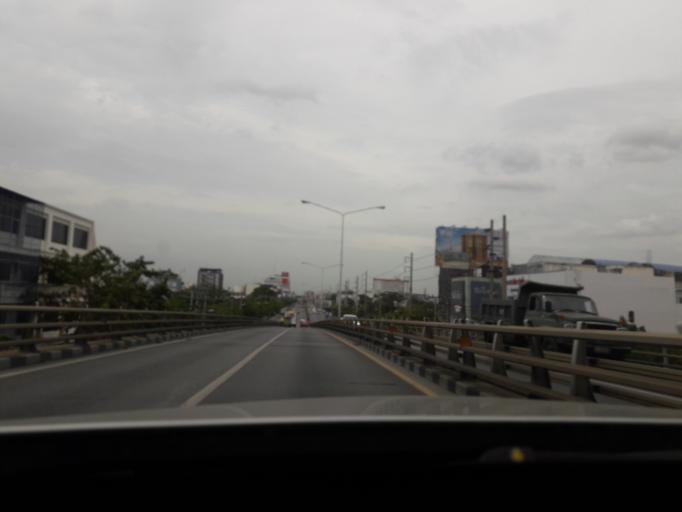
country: TH
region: Bangkok
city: Bang Phlat
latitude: 13.7849
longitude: 100.4936
